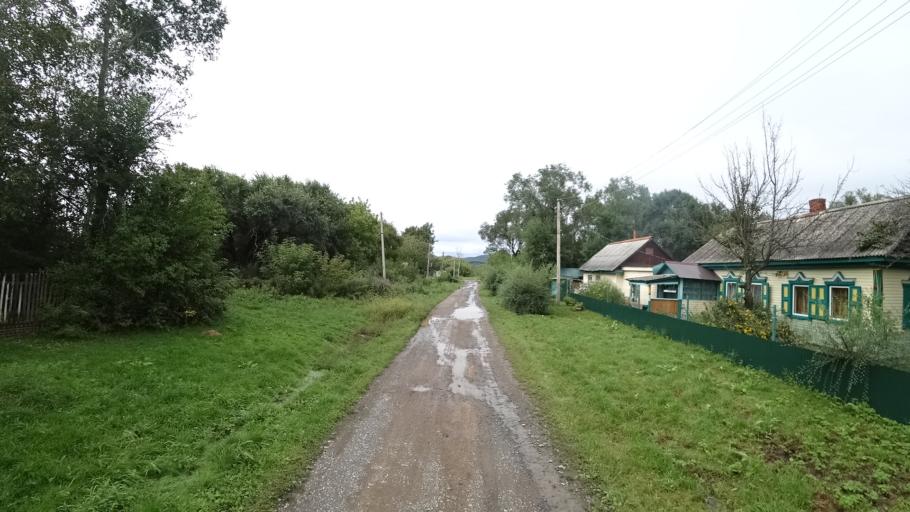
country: RU
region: Primorskiy
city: Lyalichi
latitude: 44.0794
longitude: 132.4812
